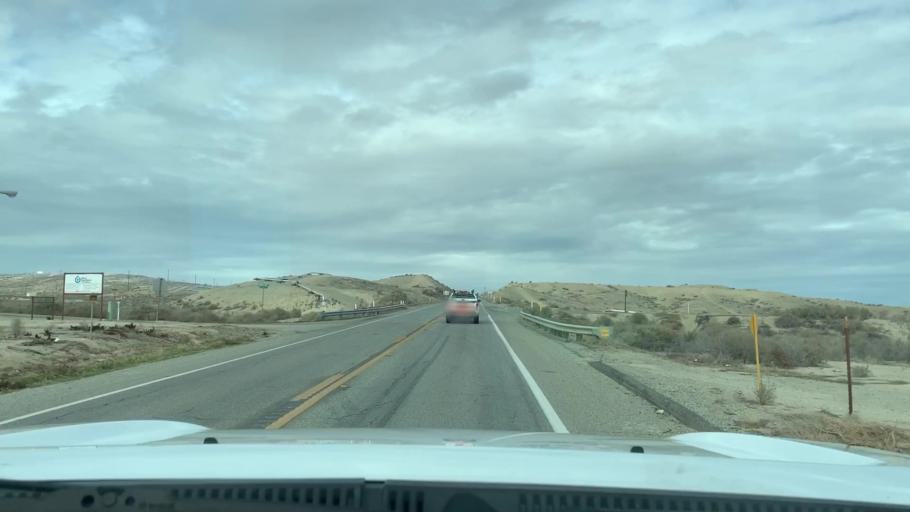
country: US
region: California
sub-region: Kern County
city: Maricopa
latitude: 35.0957
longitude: -119.4106
